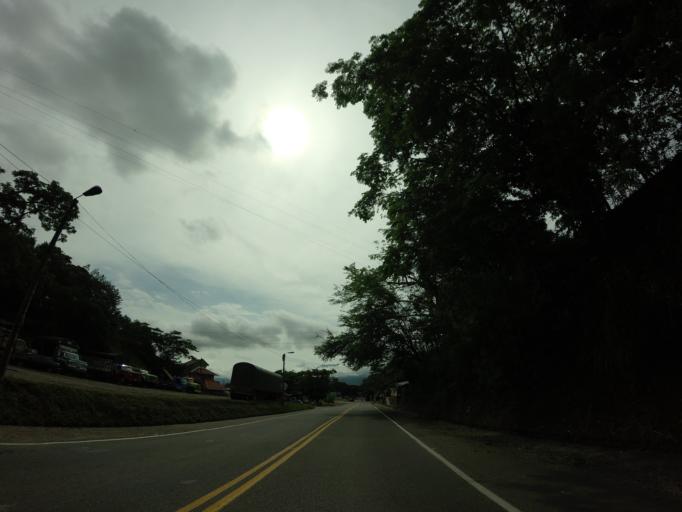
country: CO
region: Caldas
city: La Dorada
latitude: 5.4460
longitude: -74.6740
